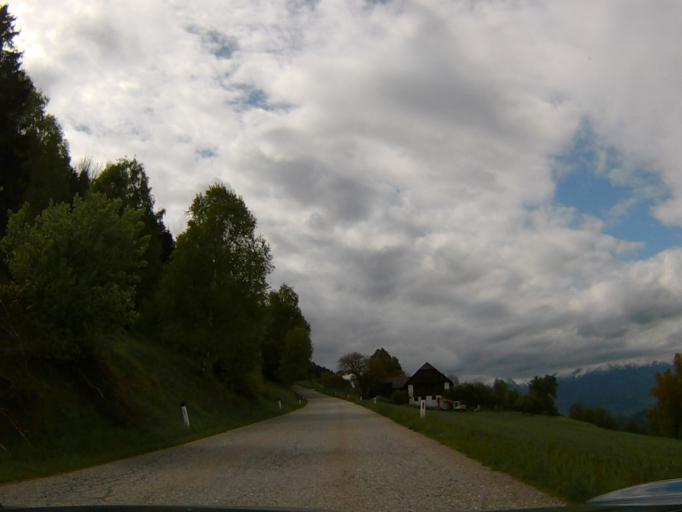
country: AT
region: Carinthia
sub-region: Politischer Bezirk Villach Land
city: Stockenboi
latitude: 46.7404
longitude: 13.5642
